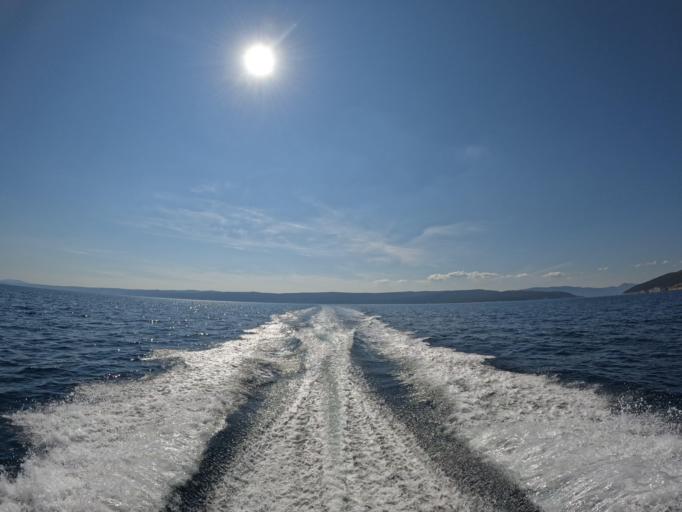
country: HR
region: Primorsko-Goranska
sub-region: Grad Krk
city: Krk
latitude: 44.9486
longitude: 14.5346
